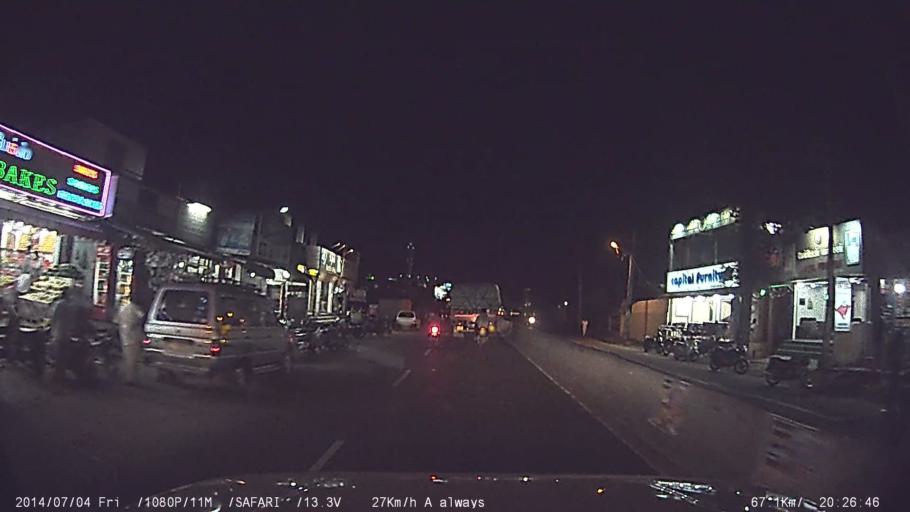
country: IN
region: Tamil Nadu
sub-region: Coimbatore
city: Coimbatore
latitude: 10.9668
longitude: 76.9556
